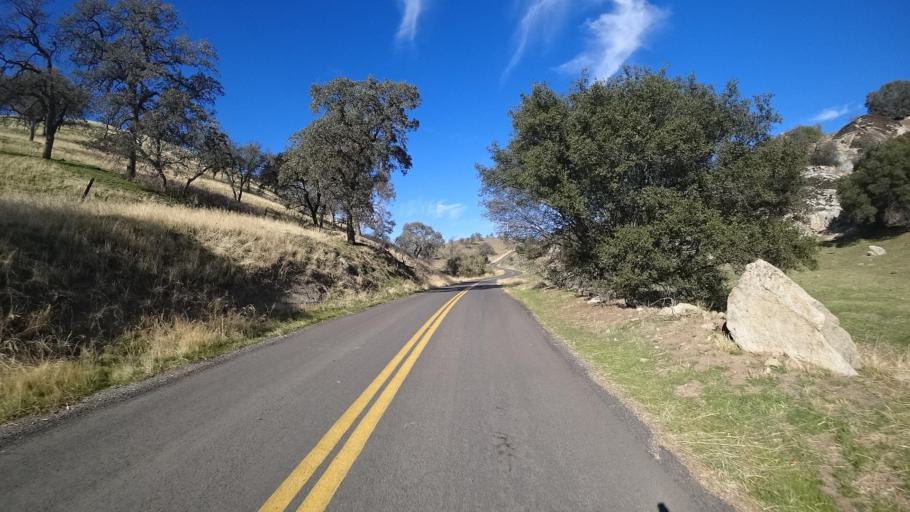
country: US
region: California
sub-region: Kern County
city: Oildale
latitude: 35.6540
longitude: -118.8406
